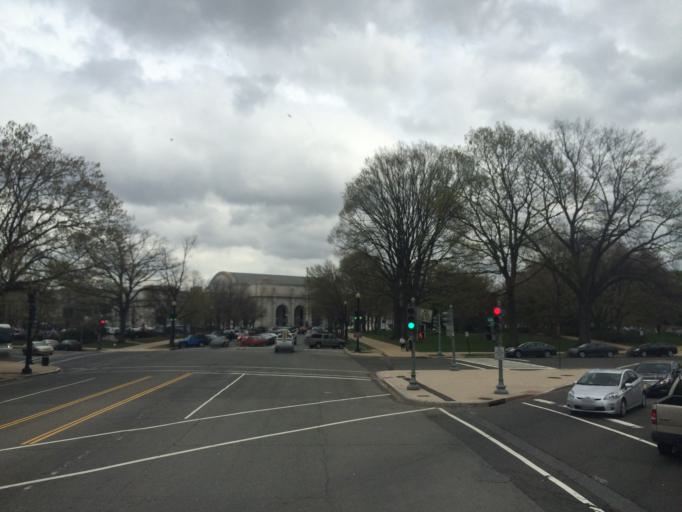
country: US
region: Washington, D.C.
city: Washington, D.C.
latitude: 38.8947
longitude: -77.0095
